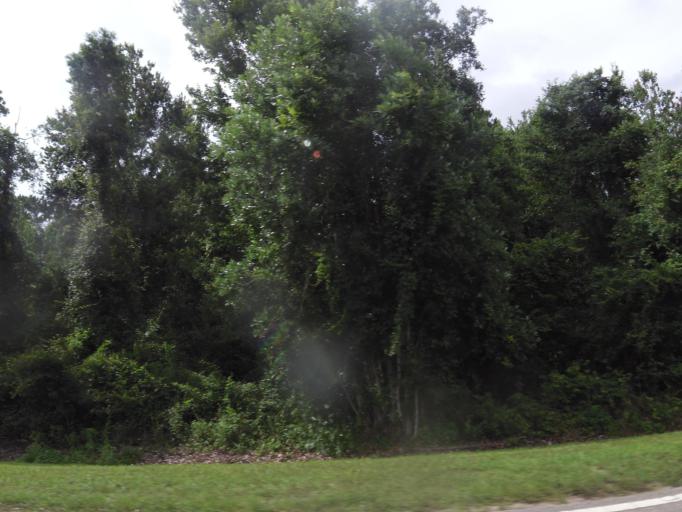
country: US
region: Florida
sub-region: Saint Johns County
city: Saint Augustine South
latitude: 29.8607
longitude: -81.4017
